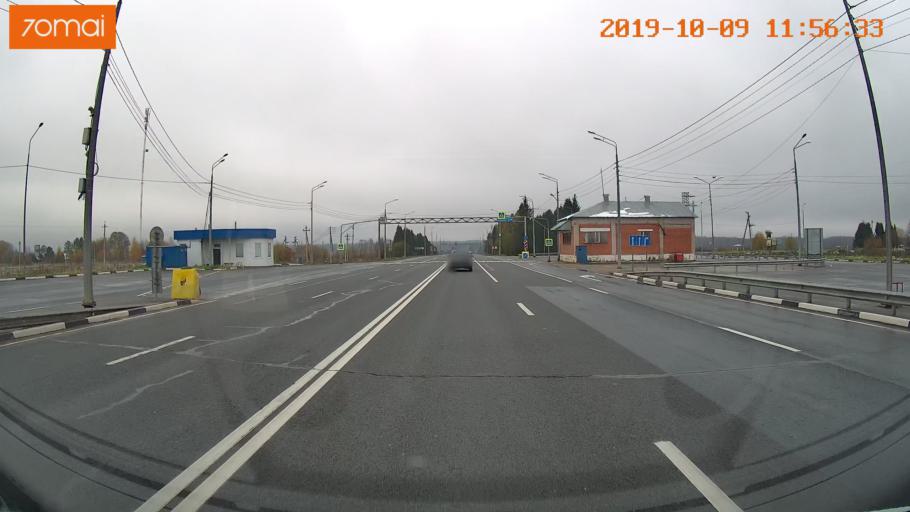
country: RU
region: Vologda
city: Gryazovets
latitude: 58.7427
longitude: 40.2882
